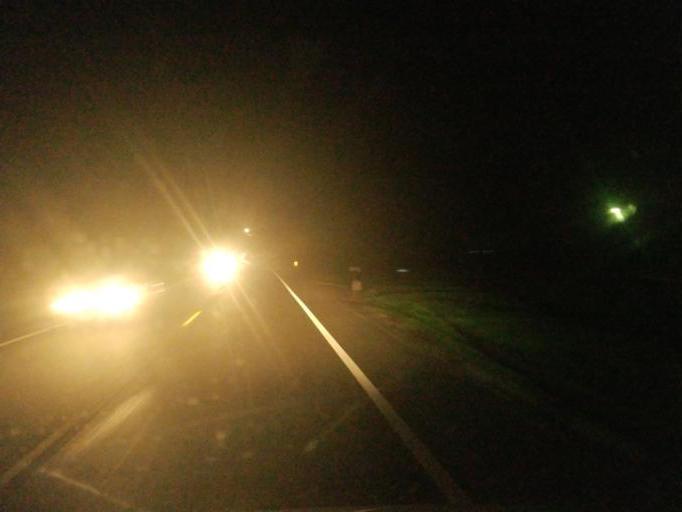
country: US
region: Ohio
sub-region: Stark County
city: East Canton
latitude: 40.7704
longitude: -81.2218
